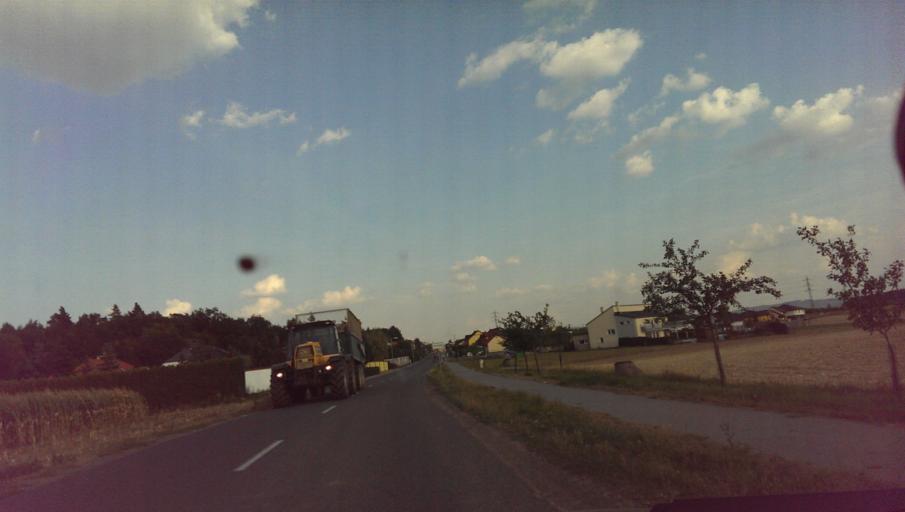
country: CZ
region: Zlin
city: Hvozdna
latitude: 49.2609
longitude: 17.7473
